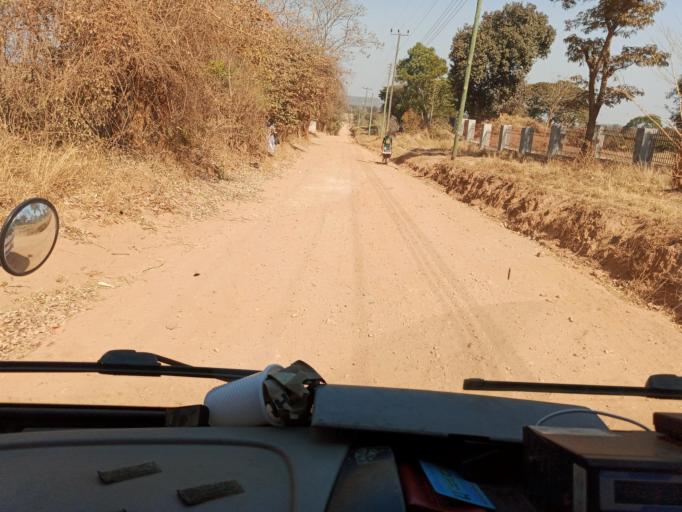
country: ZM
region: Lusaka
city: Lusaka
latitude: -15.3384
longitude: 28.1968
